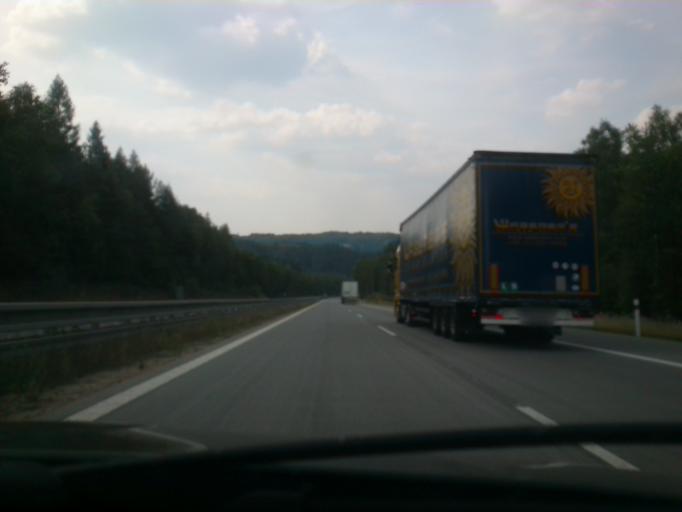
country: CZ
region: Central Bohemia
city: Divisov
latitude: 49.7711
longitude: 14.9429
